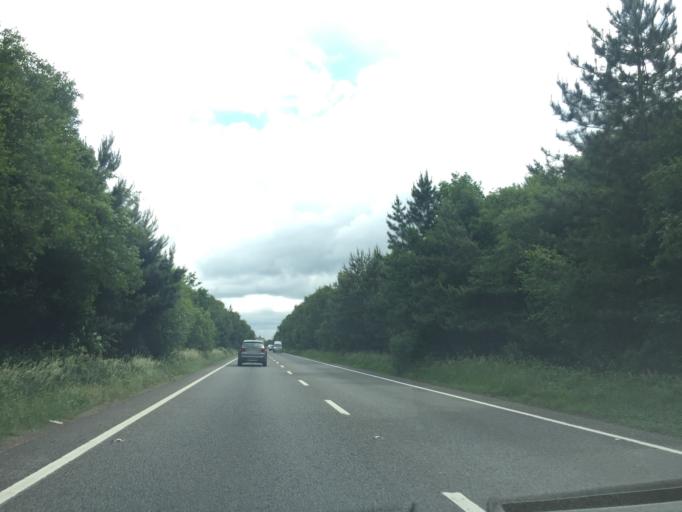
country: GB
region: England
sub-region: Dorset
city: Ferndown
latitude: 50.8145
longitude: -1.9186
